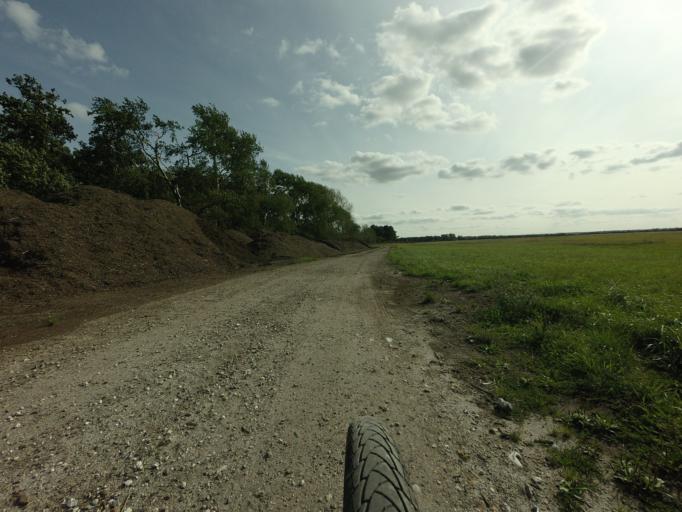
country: DK
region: Zealand
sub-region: Vordingborg Kommune
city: Praesto
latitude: 55.1492
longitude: 12.0926
